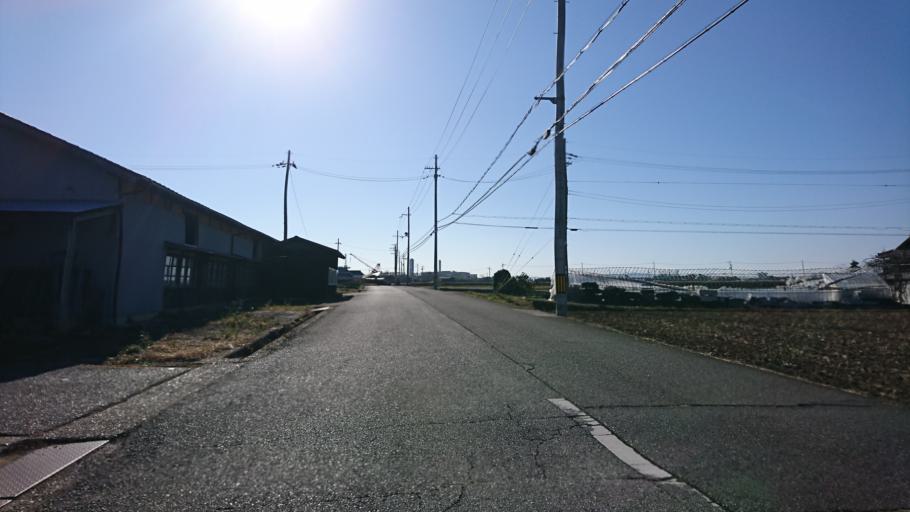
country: JP
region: Hyogo
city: Miki
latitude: 34.7206
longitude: 134.9603
